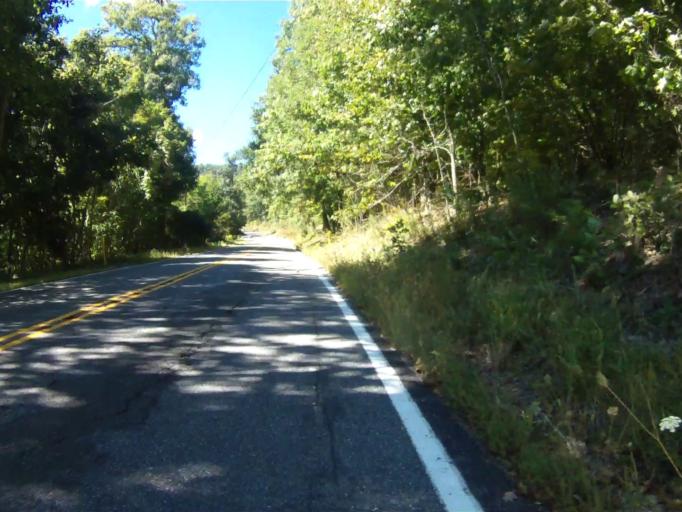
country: US
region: Pennsylvania
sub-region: Centre County
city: Park Forest Village
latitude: 40.9307
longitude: -77.9326
